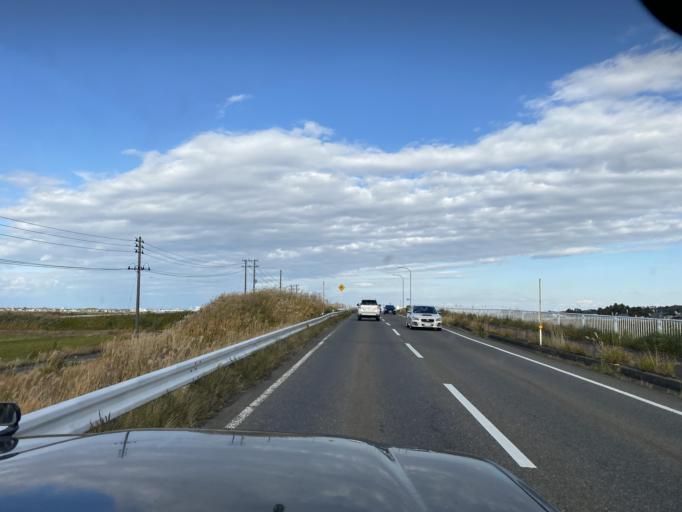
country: JP
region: Niigata
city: Niitsu-honcho
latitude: 37.7761
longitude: 139.1065
